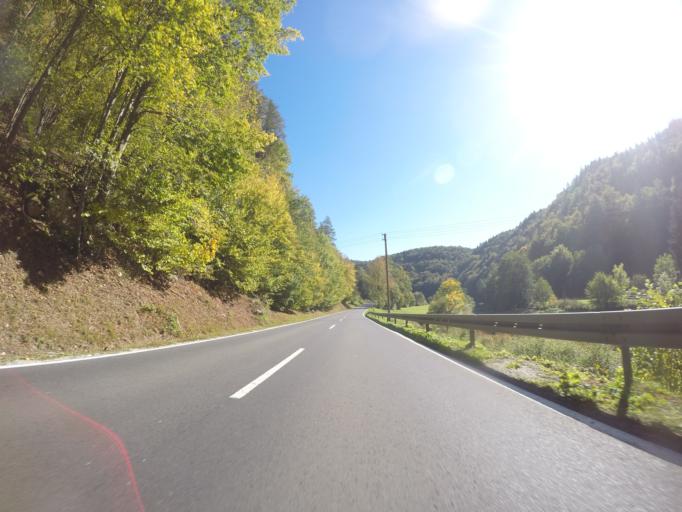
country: DE
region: Bavaria
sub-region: Upper Franconia
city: Gossweinstein
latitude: 49.7735
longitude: 11.3113
